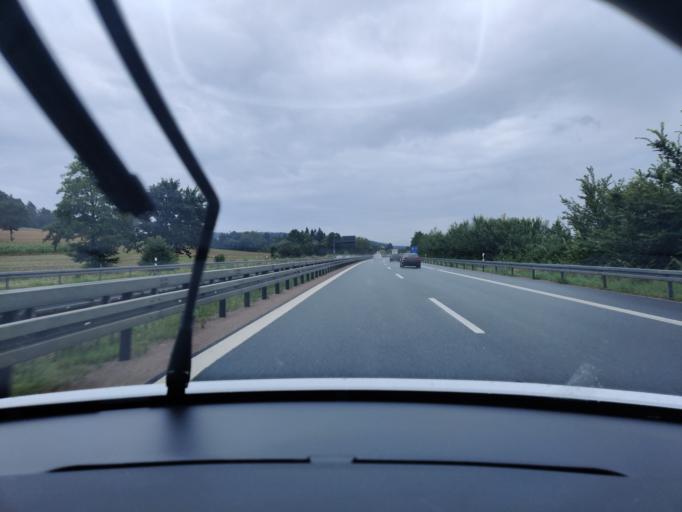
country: DE
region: Bavaria
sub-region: Upper Palatinate
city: Pfreimd
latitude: 49.5038
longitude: 12.1825
